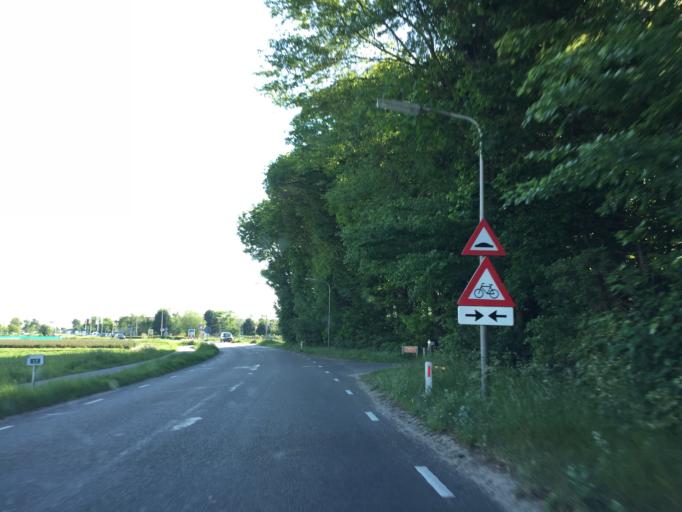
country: NL
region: South Holland
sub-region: Gemeente Noordwijk
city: Noordwijk-Binnen
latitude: 52.2521
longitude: 4.4509
